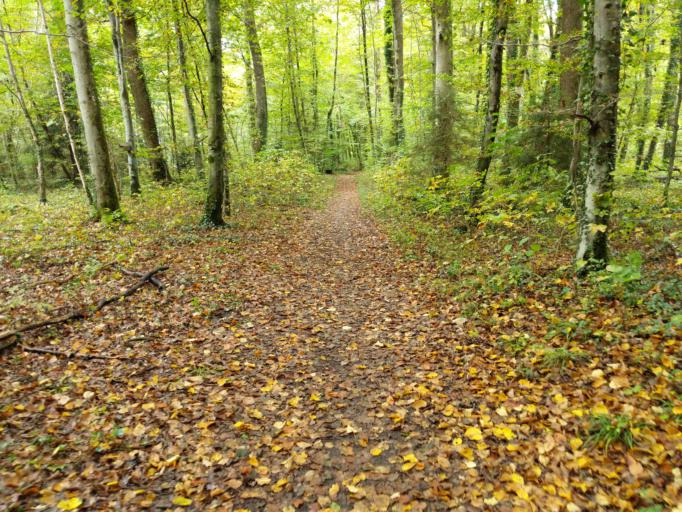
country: DE
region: Bavaria
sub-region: Upper Bavaria
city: Zorneding
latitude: 48.0910
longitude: 11.8472
